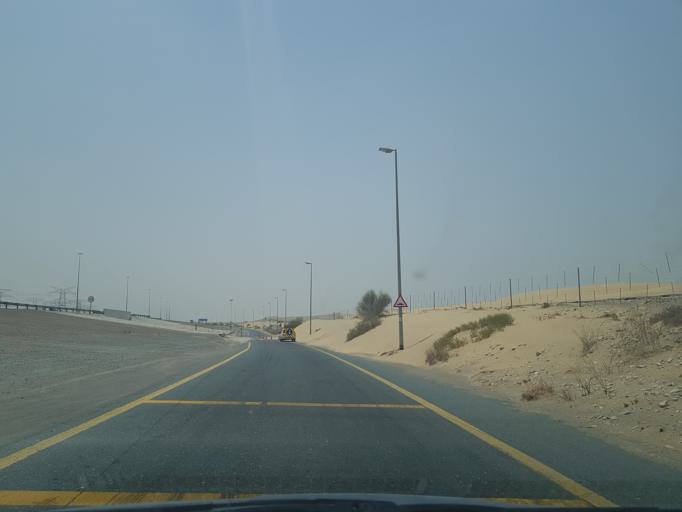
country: AE
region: Dubai
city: Dubai
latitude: 25.0612
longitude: 55.3238
